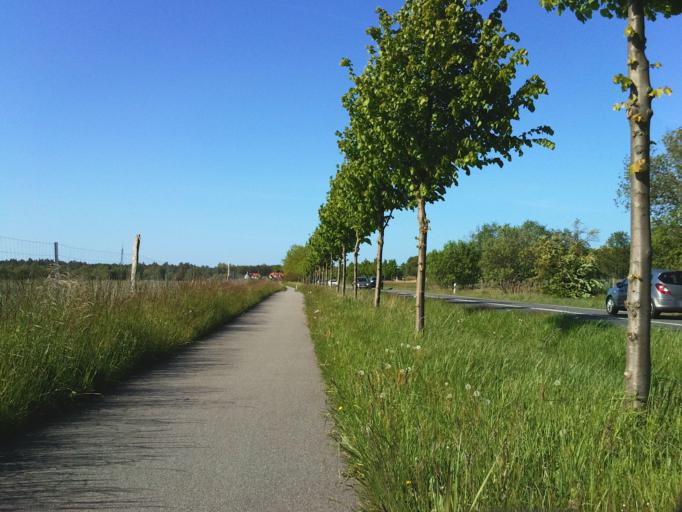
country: DE
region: Mecklenburg-Vorpommern
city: Monchhagen
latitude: 54.1811
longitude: 12.2053
